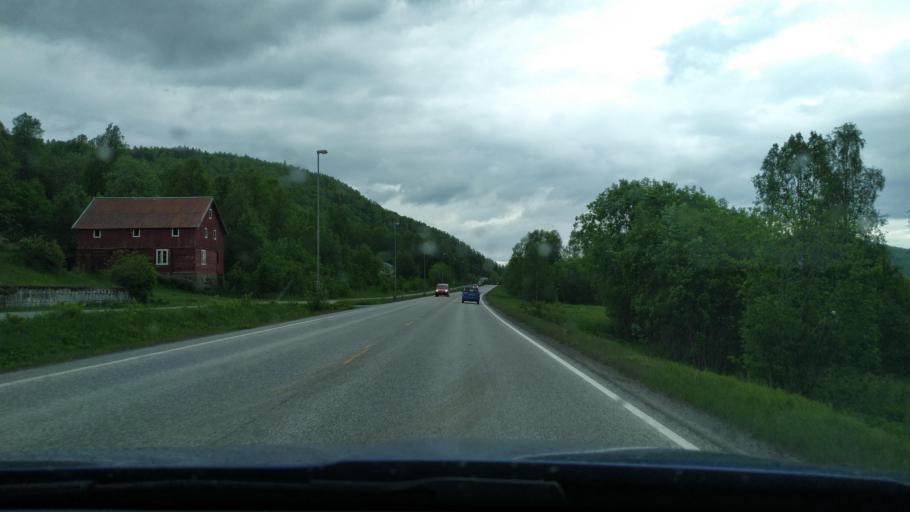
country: NO
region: Troms
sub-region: Malselv
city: Moen
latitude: 69.0188
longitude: 18.4863
